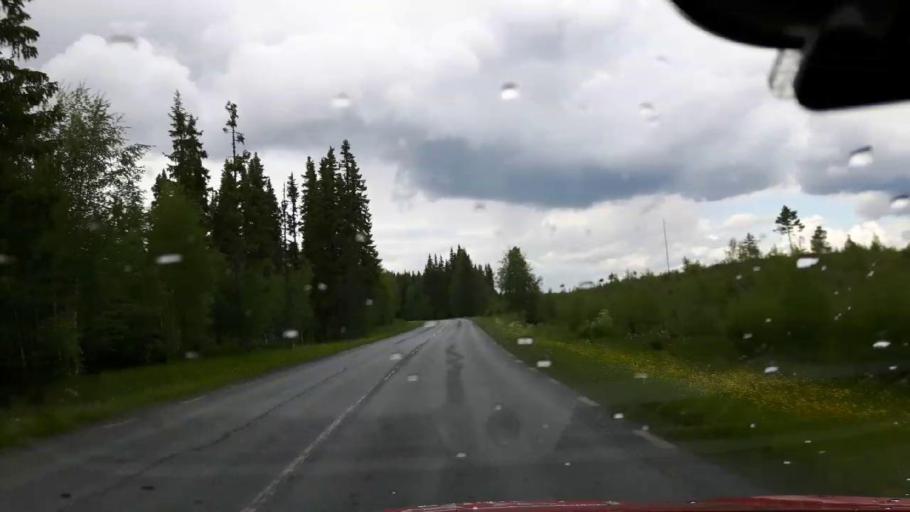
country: SE
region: Jaemtland
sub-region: Krokoms Kommun
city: Krokom
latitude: 63.4126
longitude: 14.2381
